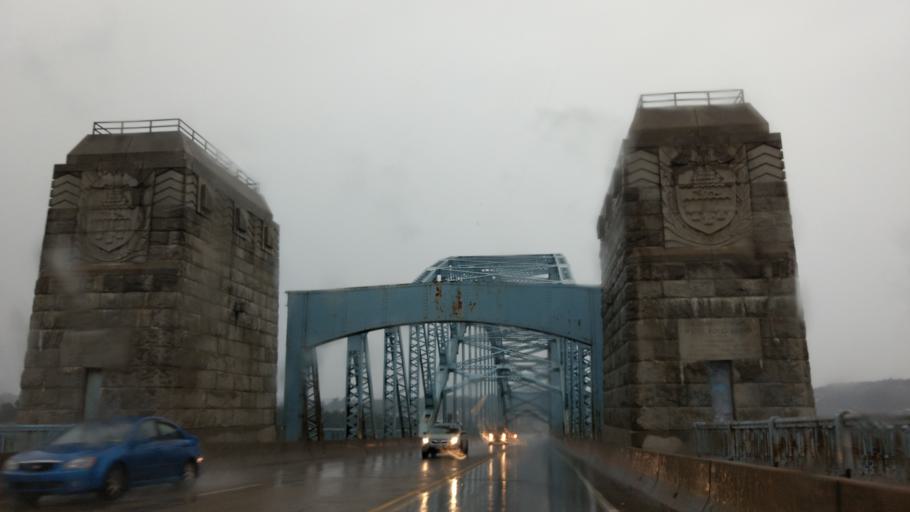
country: US
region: Pennsylvania
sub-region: Allegheny County
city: Bellevue
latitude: 40.4776
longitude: -80.0469
